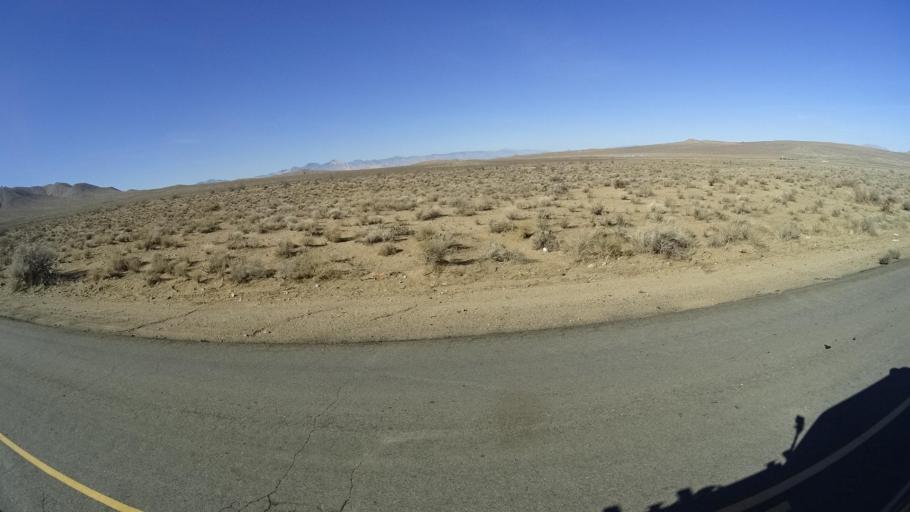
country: US
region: California
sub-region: Kern County
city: Ridgecrest
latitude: 35.4824
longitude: -117.6430
